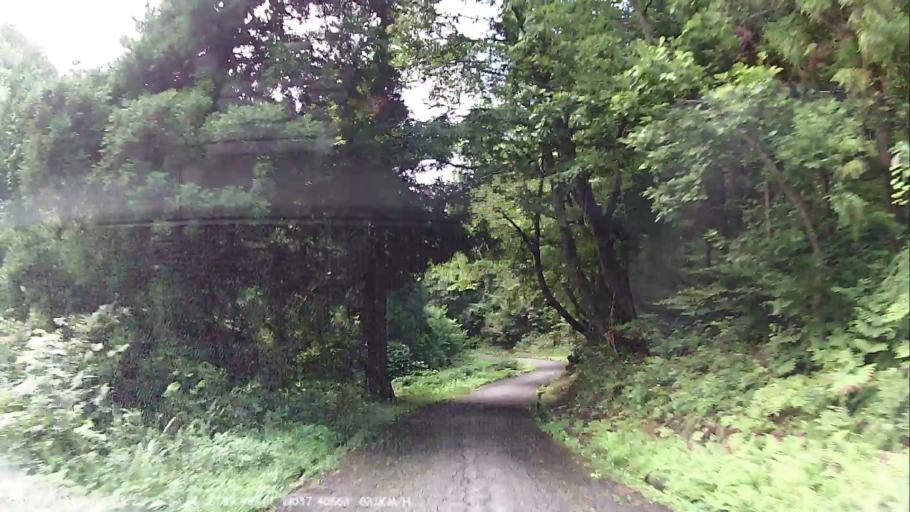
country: JP
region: Fukushima
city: Inawashiro
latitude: 37.4066
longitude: 139.9574
